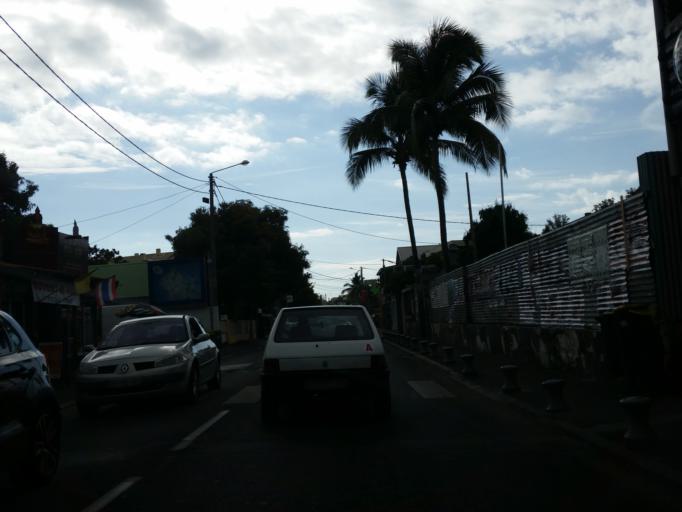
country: RE
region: Reunion
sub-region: Reunion
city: Saint-Paul
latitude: -21.0519
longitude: 55.2273
